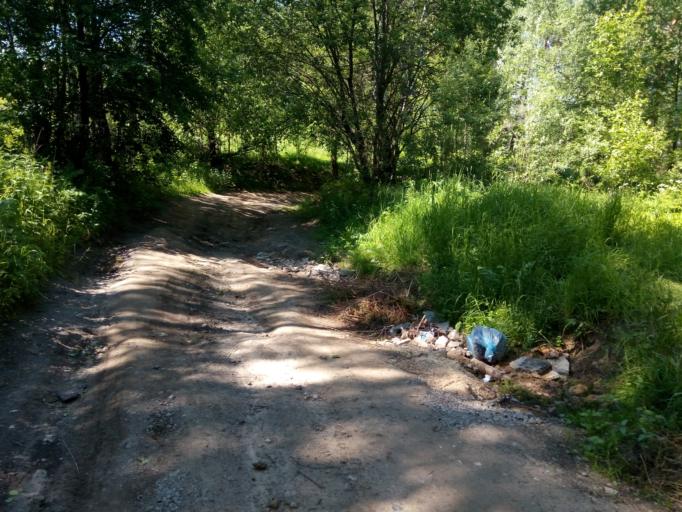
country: RU
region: Nizjnij Novgorod
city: Voskresenskoye
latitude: 56.7843
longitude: 45.5224
